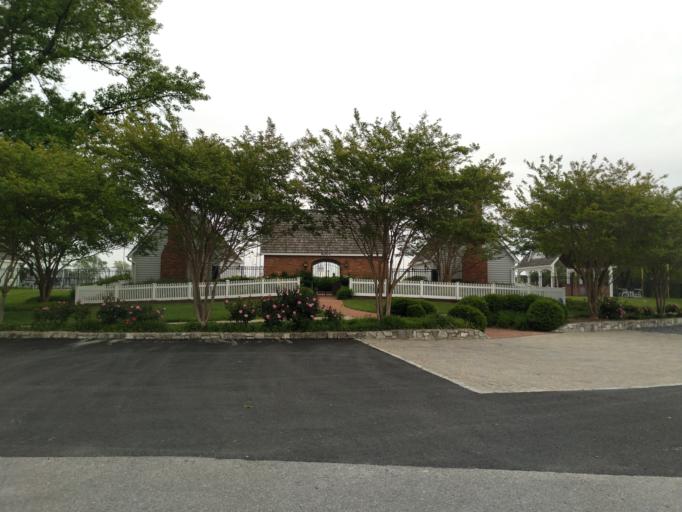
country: US
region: Maryland
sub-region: Anne Arundel County
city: Deale
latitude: 38.7751
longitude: -76.5653
